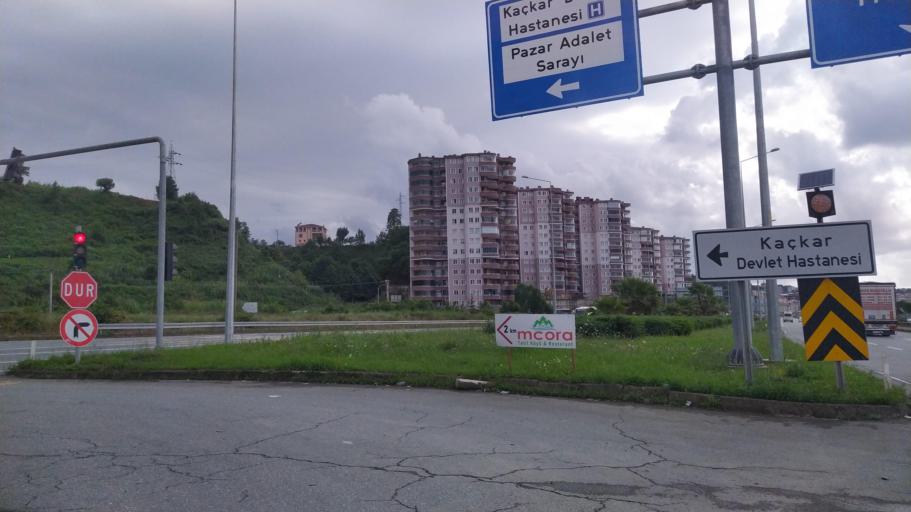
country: TR
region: Rize
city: Pazar
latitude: 41.1761
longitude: 40.9302
